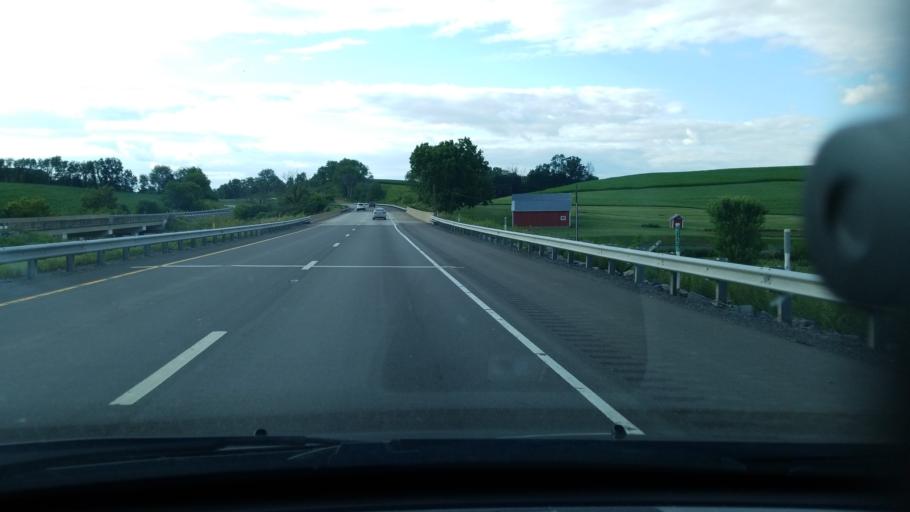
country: US
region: Pennsylvania
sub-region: Northumberland County
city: Milton
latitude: 41.0385
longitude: -76.8102
